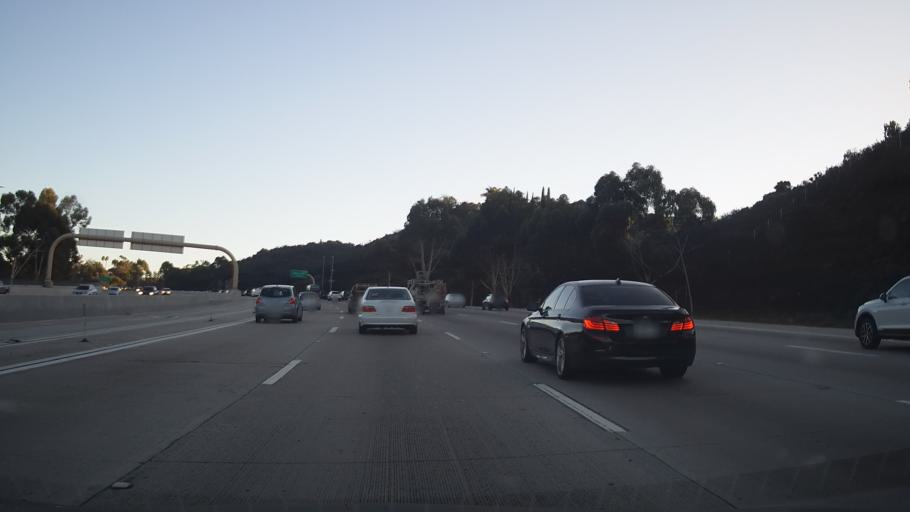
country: US
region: California
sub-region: San Diego County
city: San Diego
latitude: 32.7733
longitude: -117.1128
